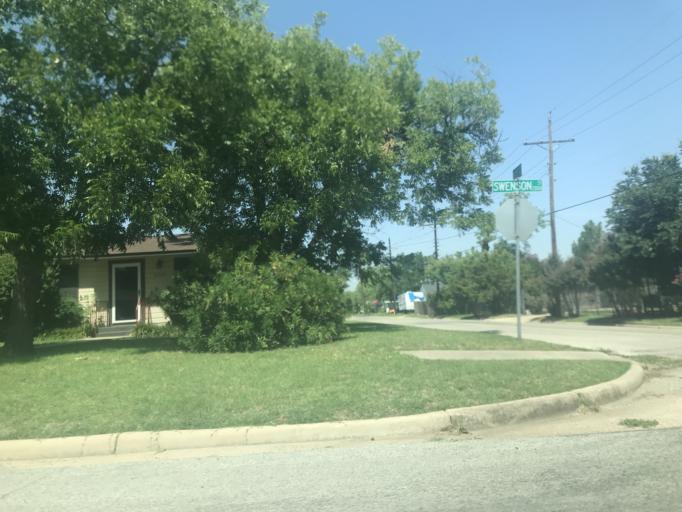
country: US
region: Texas
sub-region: Taylor County
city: Abilene
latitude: 32.4728
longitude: -99.7406
